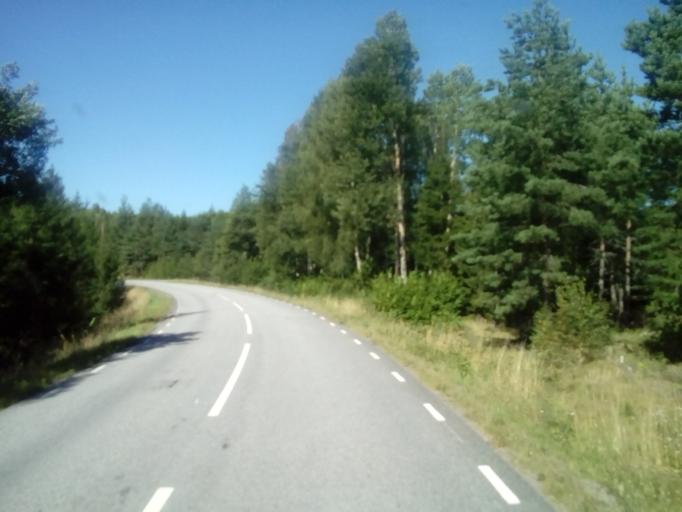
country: SE
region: Kalmar
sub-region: Vimmerby Kommun
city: Sodra Vi
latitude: 57.9059
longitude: 16.0181
